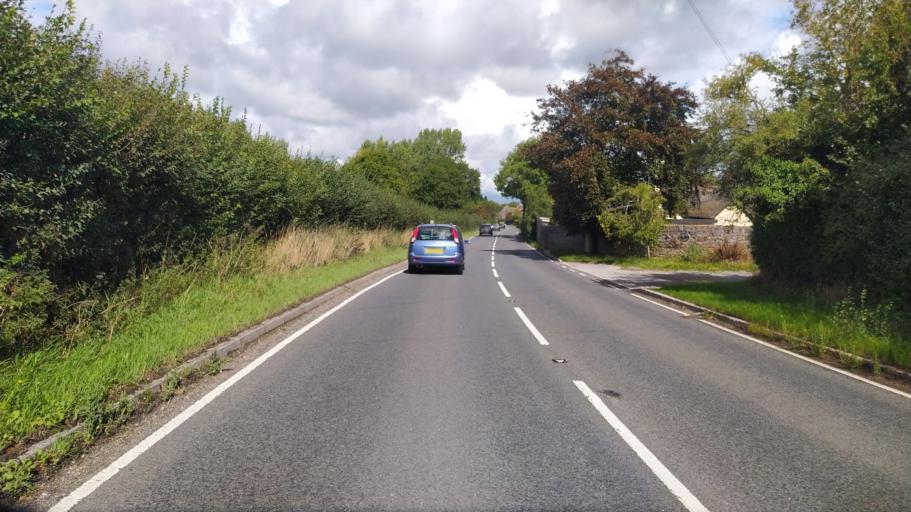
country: GB
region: England
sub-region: Dorset
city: Sturminster Newton
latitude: 50.9142
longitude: -2.2769
